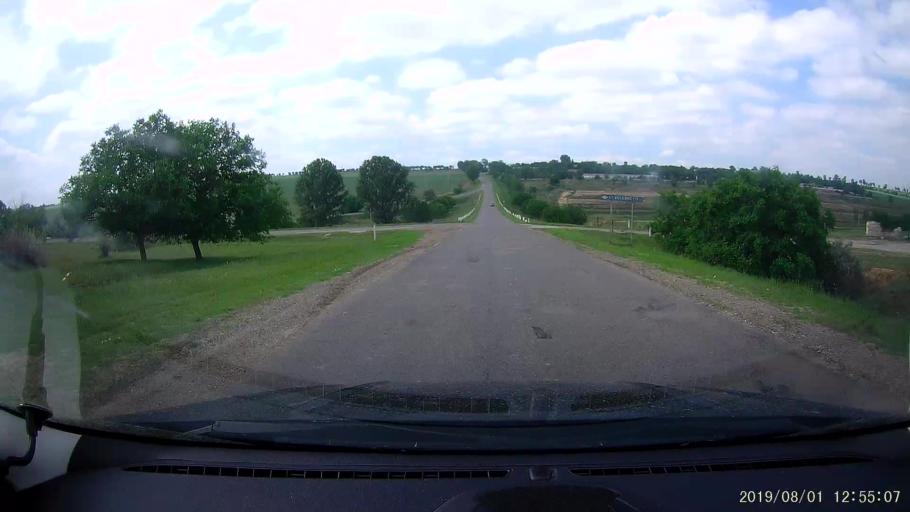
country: MD
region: Gagauzia
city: Vulcanesti
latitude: 45.6944
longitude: 28.4734
